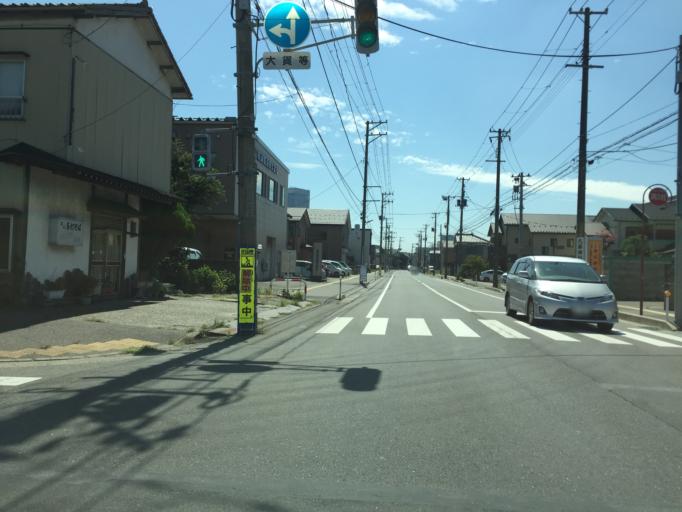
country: JP
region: Niigata
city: Niigata-shi
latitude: 37.9350
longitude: 139.0570
